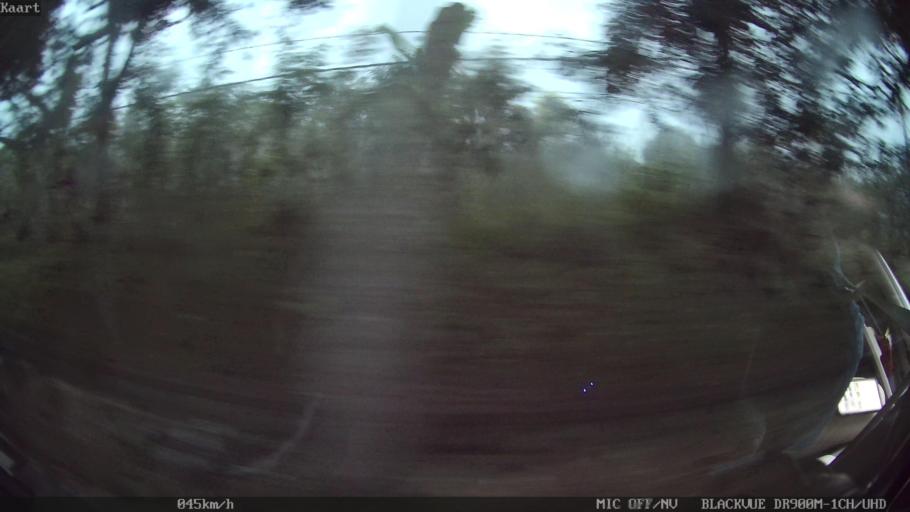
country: ID
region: Bali
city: Banjar Taro Kelod
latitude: -8.3286
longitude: 115.2903
